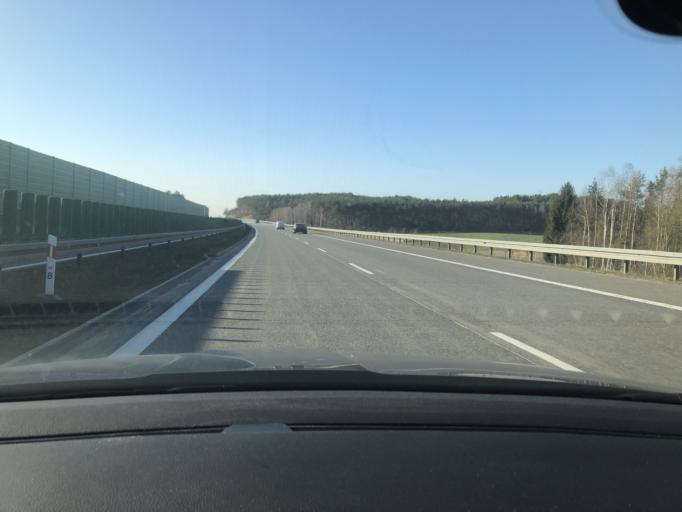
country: PL
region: Lubusz
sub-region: Powiat sulecinski
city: Torzym
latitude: 52.3324
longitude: 15.0215
